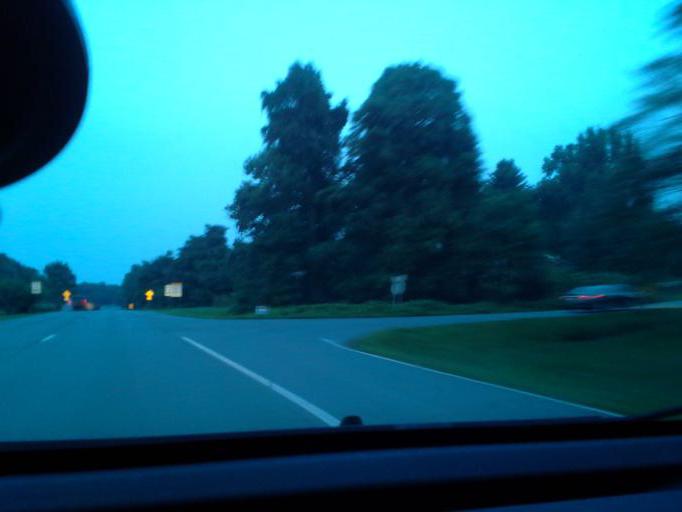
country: US
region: Maryland
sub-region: Calvert County
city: Chesapeake Beach
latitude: 38.6987
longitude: -76.5502
